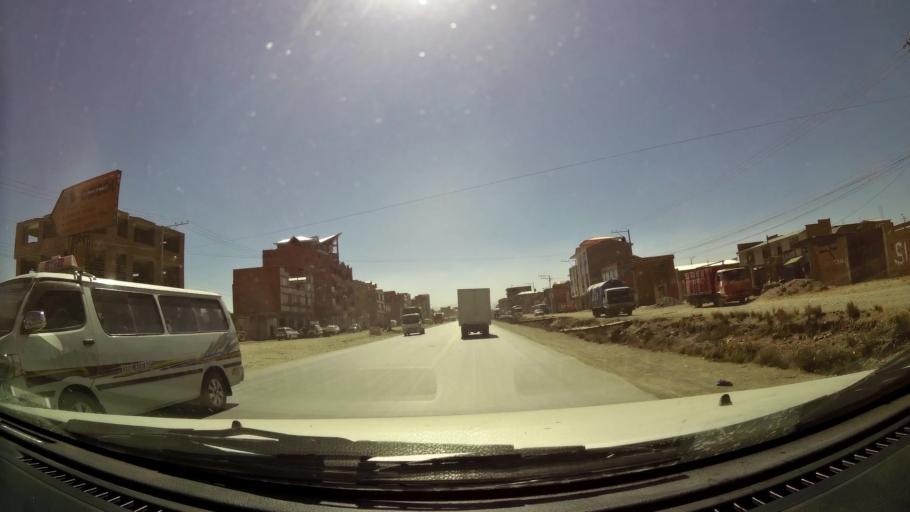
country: BO
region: La Paz
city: La Paz
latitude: -16.5528
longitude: -68.2075
